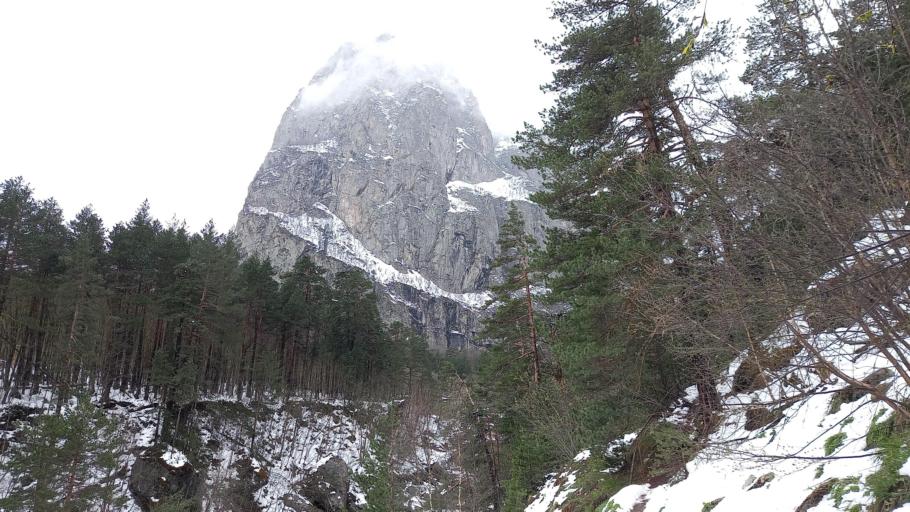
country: RU
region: North Ossetia
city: Mizur
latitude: 42.7902
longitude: 43.9026
